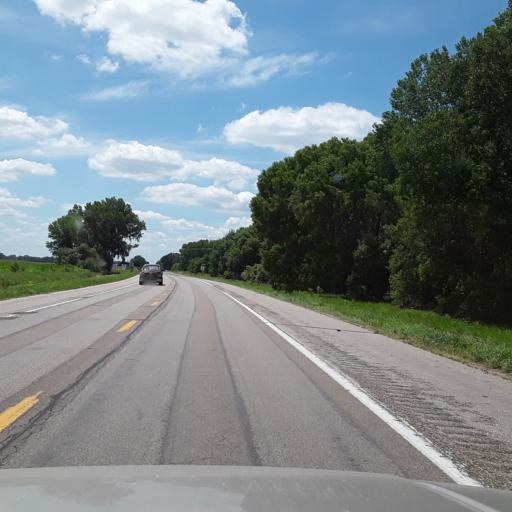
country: US
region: Nebraska
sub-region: Platte County
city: Columbus
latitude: 41.3857
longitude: -97.4996
